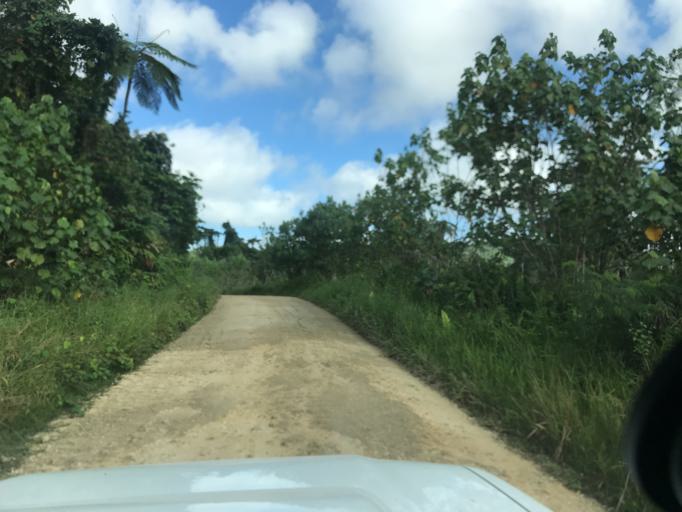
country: VU
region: Sanma
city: Luganville
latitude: -15.4749
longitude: 167.0726
